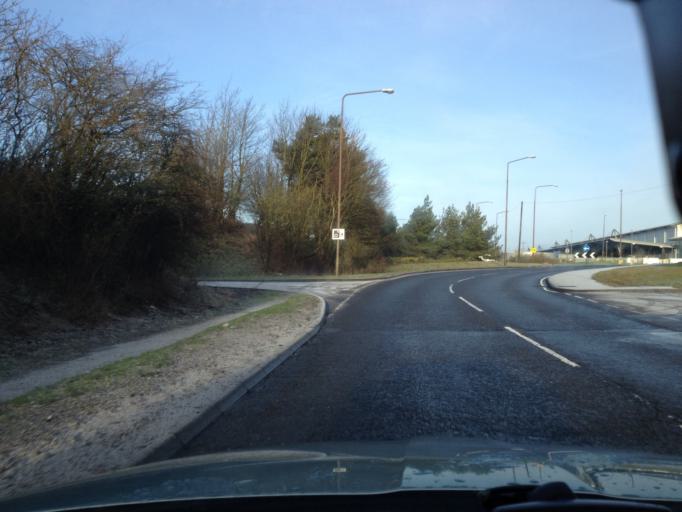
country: GB
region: Scotland
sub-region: West Lothian
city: Blackburn
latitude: 55.8758
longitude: -3.6537
